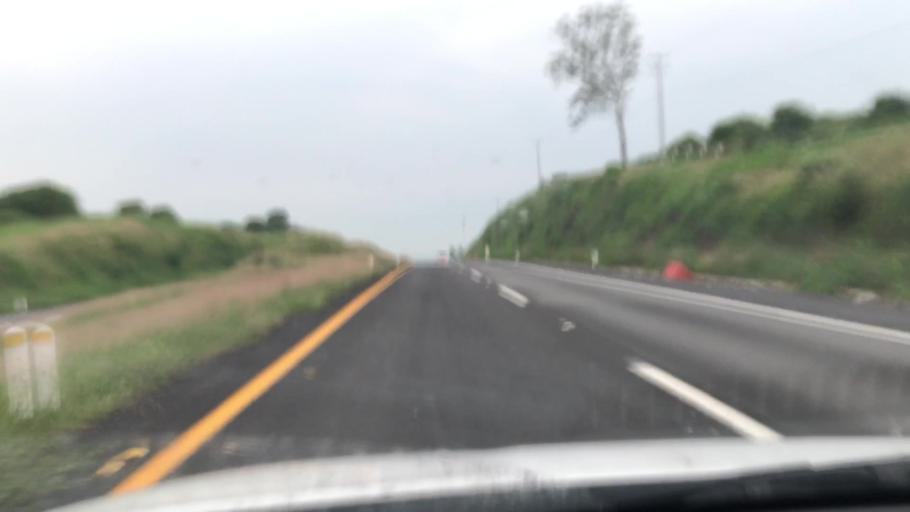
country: MX
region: Jalisco
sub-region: Zapotlanejo
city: La Mezquitera
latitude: 20.5552
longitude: -103.0590
